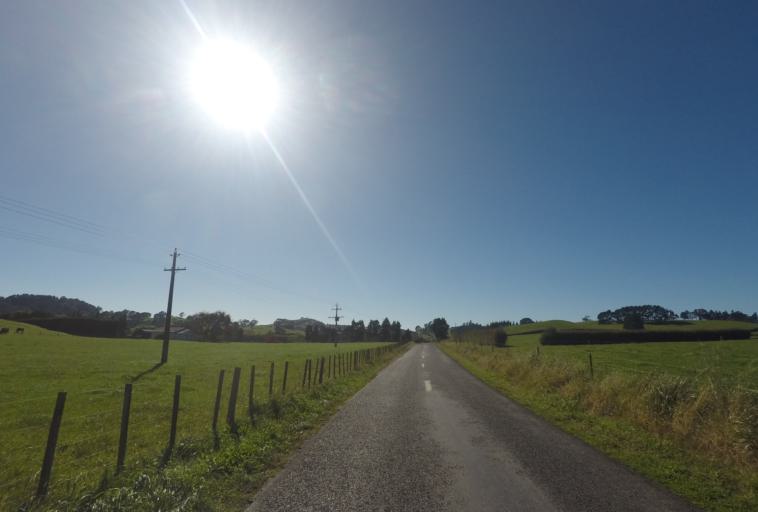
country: NZ
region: Bay of Plenty
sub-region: Western Bay of Plenty District
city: Waihi Beach
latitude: -37.4123
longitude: 175.8911
